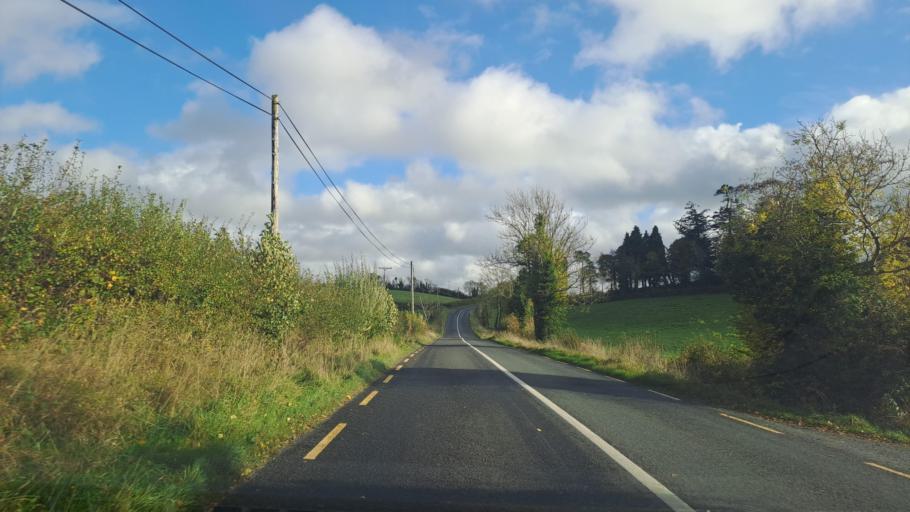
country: IE
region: Ulster
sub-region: County Monaghan
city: Monaghan
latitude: 54.1307
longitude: -6.9310
